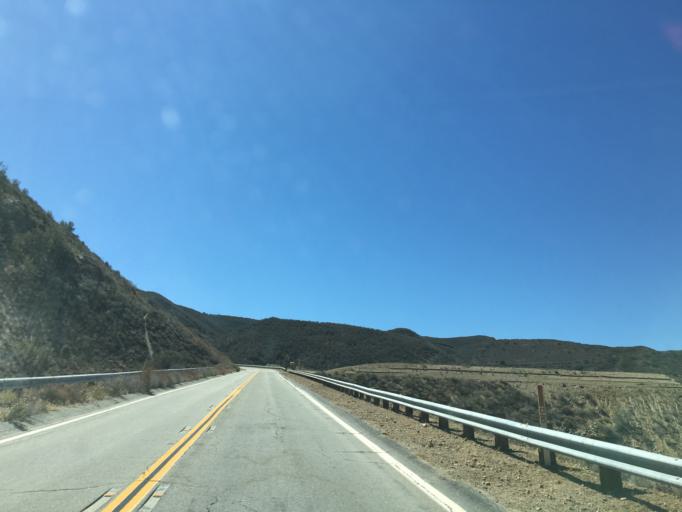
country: US
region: California
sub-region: Los Angeles County
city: Castaic
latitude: 34.5693
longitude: -118.5581
